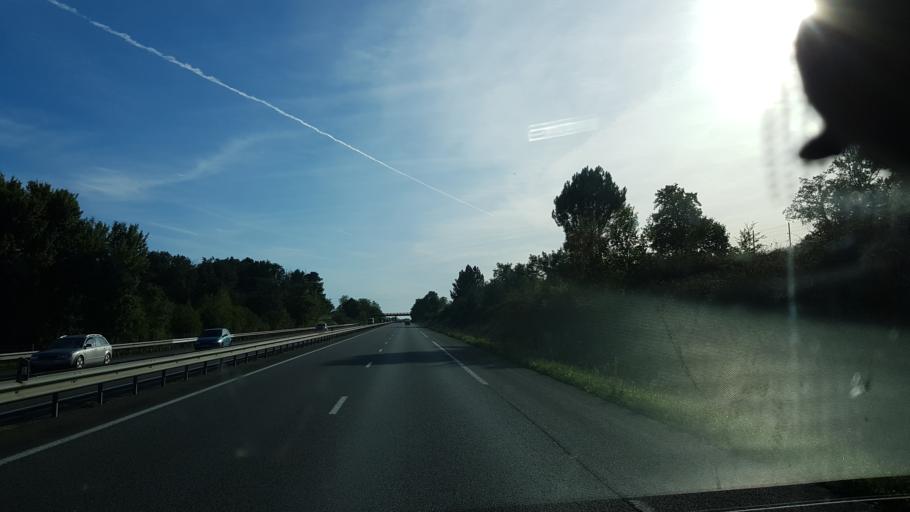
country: FR
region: Poitou-Charentes
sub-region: Departement de la Charente-Maritime
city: Chevanceaux
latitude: 45.2813
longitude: -0.2432
